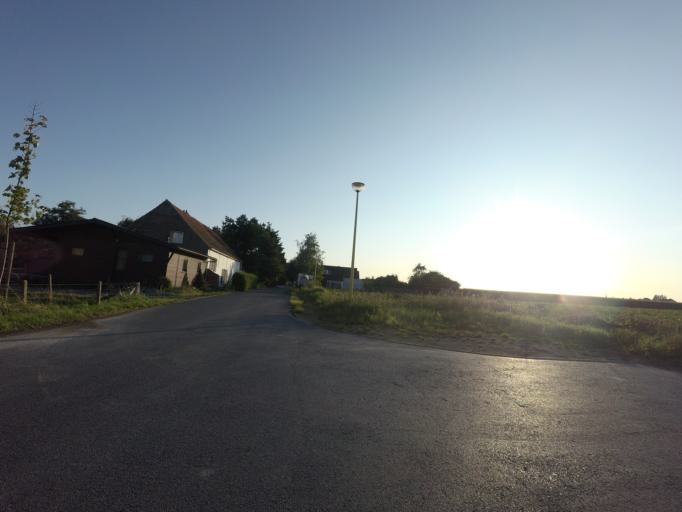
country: BE
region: Flanders
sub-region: Provincie Vlaams-Brabant
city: Londerzeel
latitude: 50.9992
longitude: 4.3287
